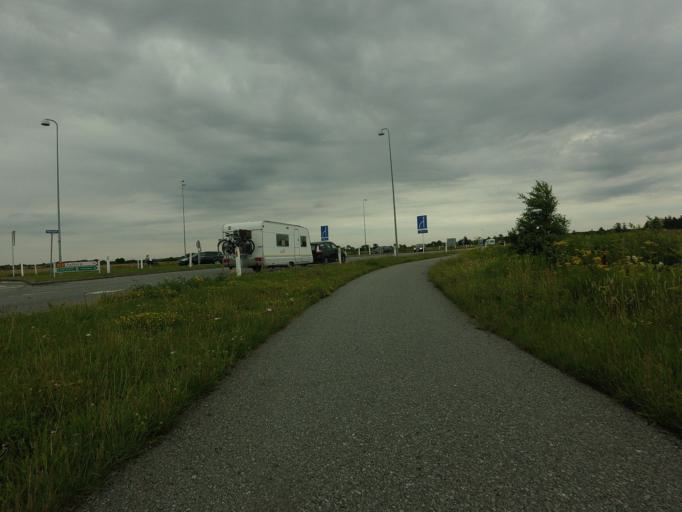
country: DK
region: North Denmark
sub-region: Alborg Kommune
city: Vadum
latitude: 57.1019
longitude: 9.8862
